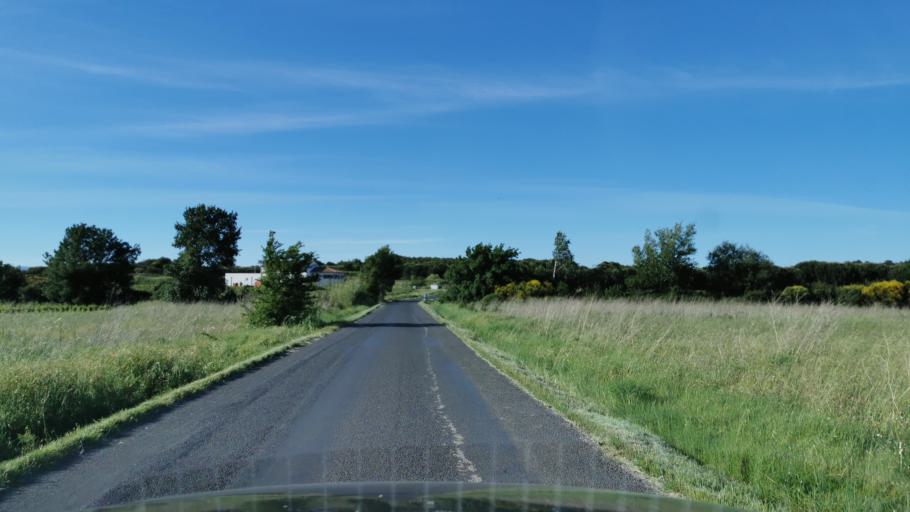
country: FR
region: Languedoc-Roussillon
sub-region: Departement de l'Aude
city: Nevian
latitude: 43.2164
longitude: 2.9126
